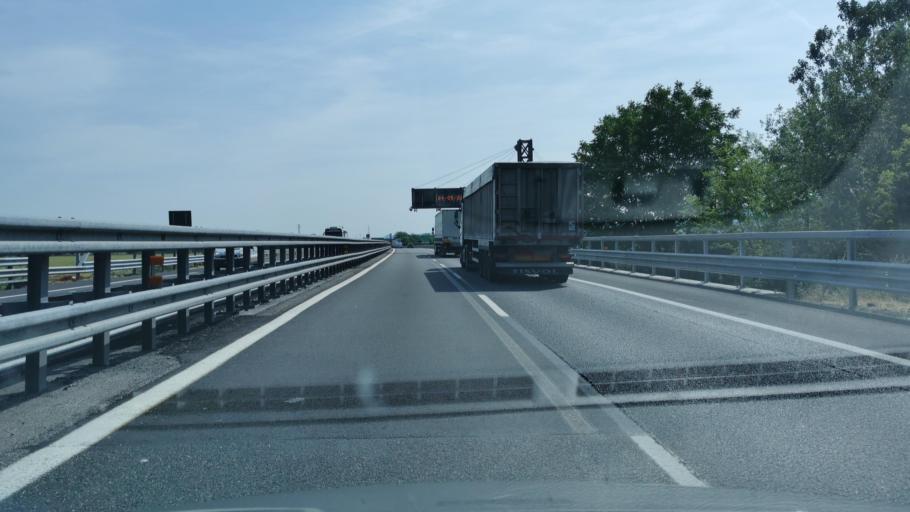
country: IT
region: Lombardy
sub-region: Provincia di Pavia
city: Verretto
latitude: 45.0344
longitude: 9.1194
